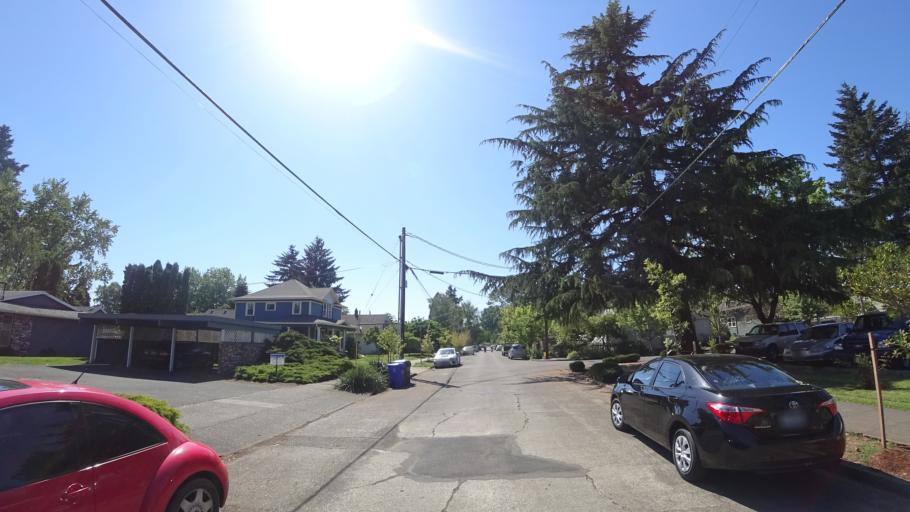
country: US
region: Oregon
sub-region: Multnomah County
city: Lents
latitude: 45.4924
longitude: -122.6050
